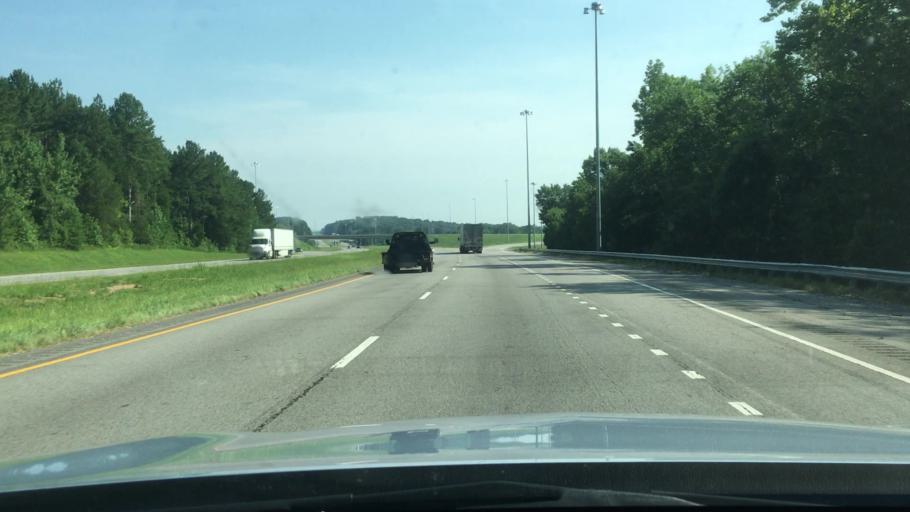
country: US
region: Alabama
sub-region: DeKalb County
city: Fort Payne
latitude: 34.4996
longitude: -85.6941
